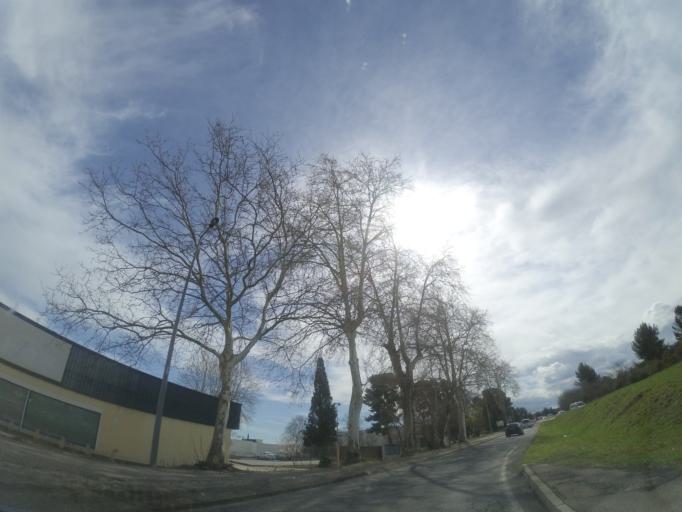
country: FR
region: Languedoc-Roussillon
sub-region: Departement des Pyrenees-Orientales
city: Perpignan
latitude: 42.6731
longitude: 2.8847
